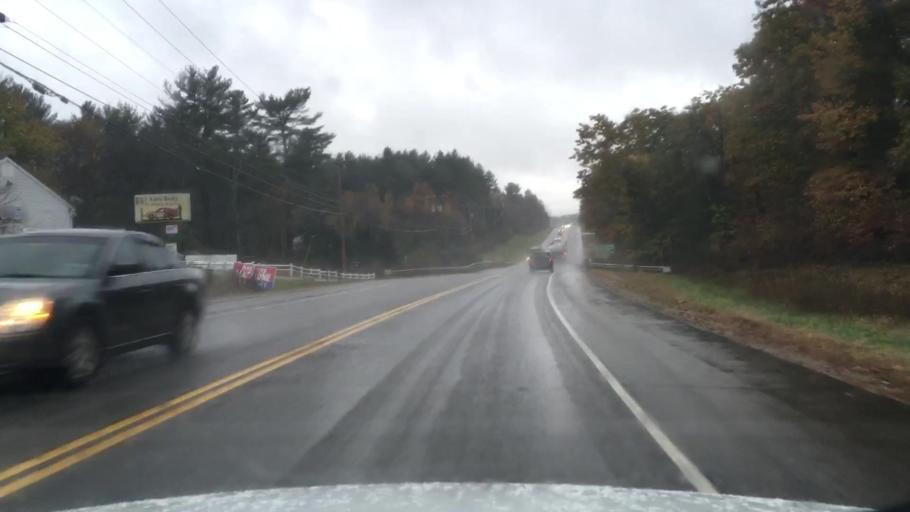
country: US
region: New Hampshire
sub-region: Strafford County
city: Rochester
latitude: 43.2493
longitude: -70.9813
